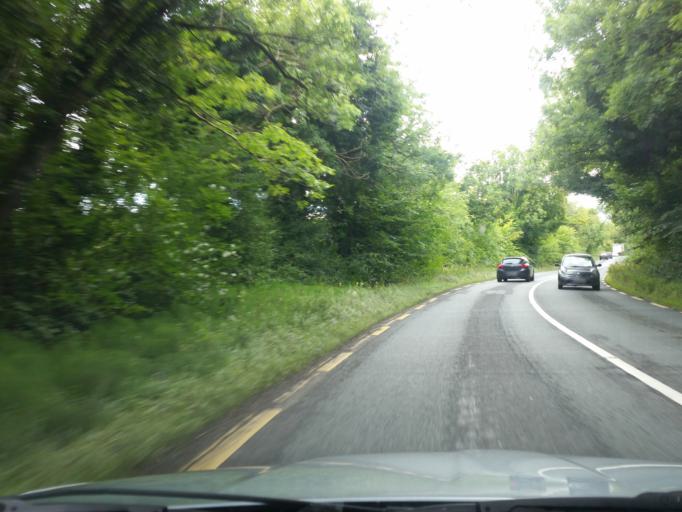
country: IE
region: Ulster
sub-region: An Cabhan
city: Belturbet
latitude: 54.1104
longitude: -7.3559
